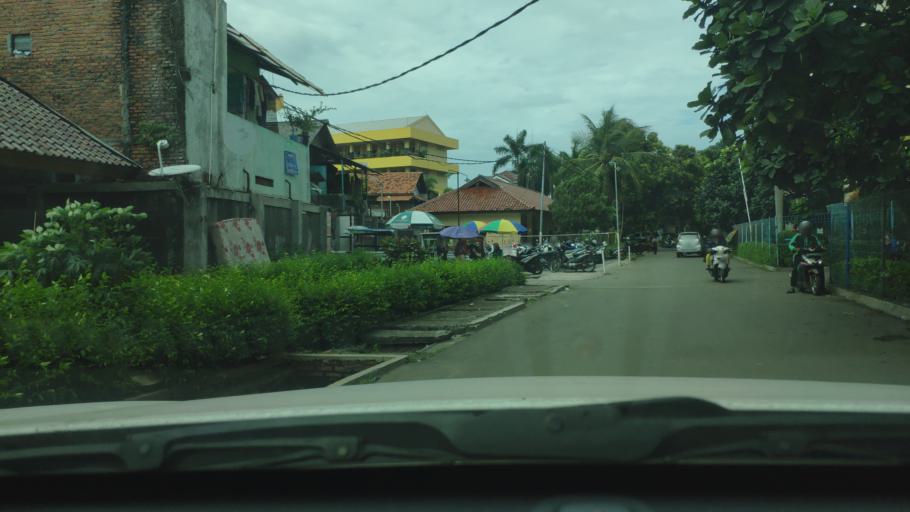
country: ID
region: West Java
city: Ciputat
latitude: -6.2223
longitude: 106.7076
